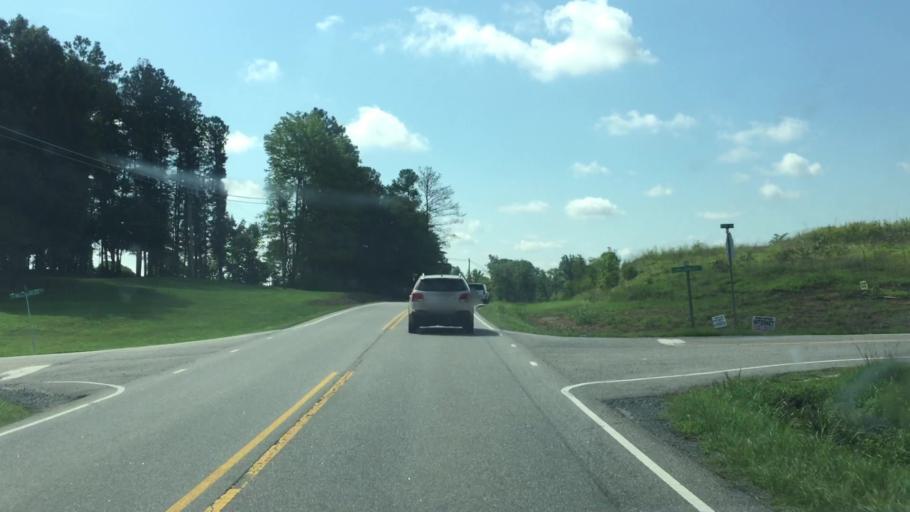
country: US
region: North Carolina
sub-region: Anson County
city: Polkton
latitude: 35.0171
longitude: -80.2200
